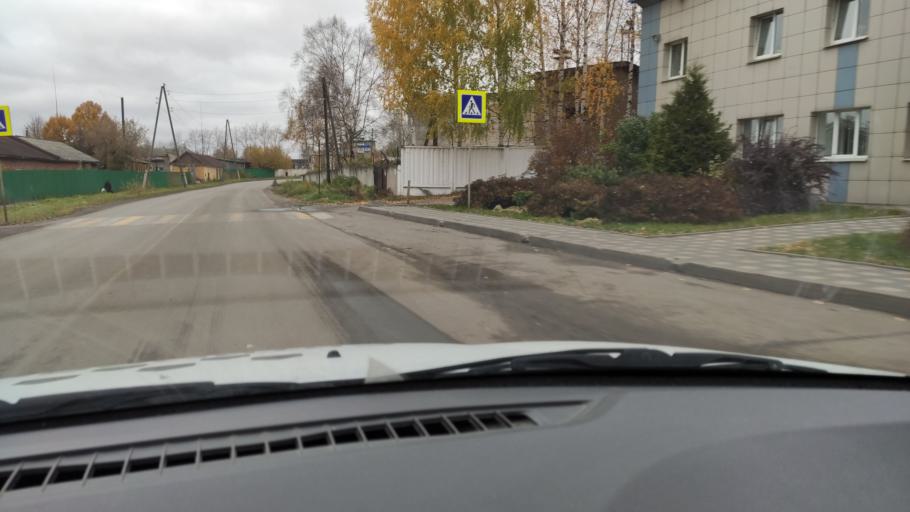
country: RU
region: Kirov
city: Slobodskoy
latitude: 58.7211
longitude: 50.1747
